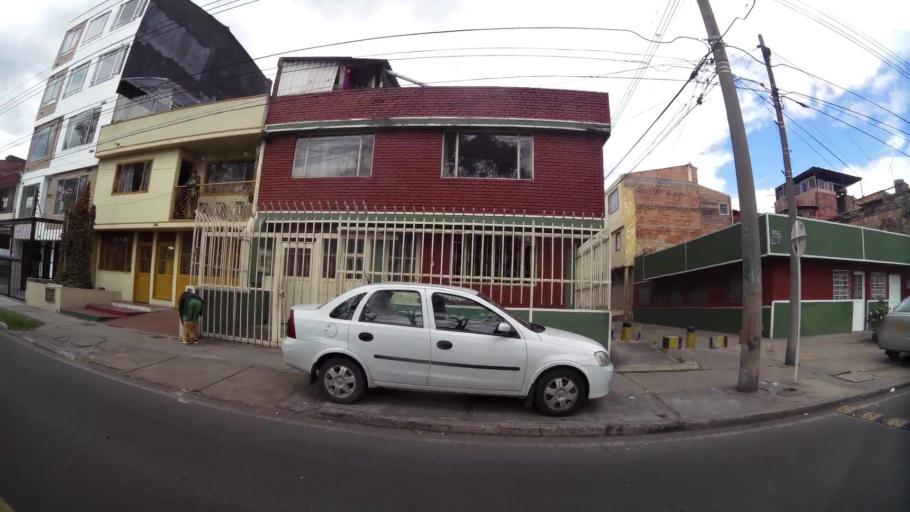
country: CO
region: Bogota D.C.
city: Bogota
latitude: 4.5982
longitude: -74.1257
